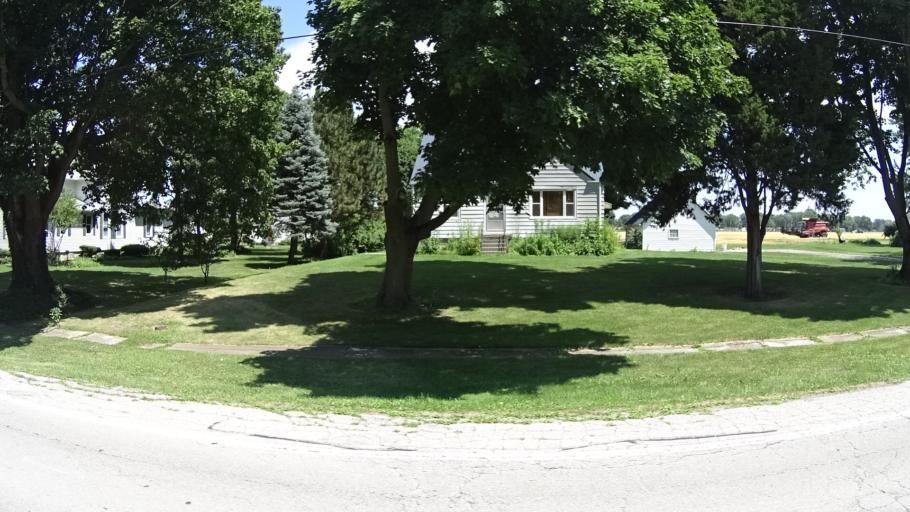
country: US
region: Ohio
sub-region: Erie County
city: Sandusky
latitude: 41.4379
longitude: -82.7725
